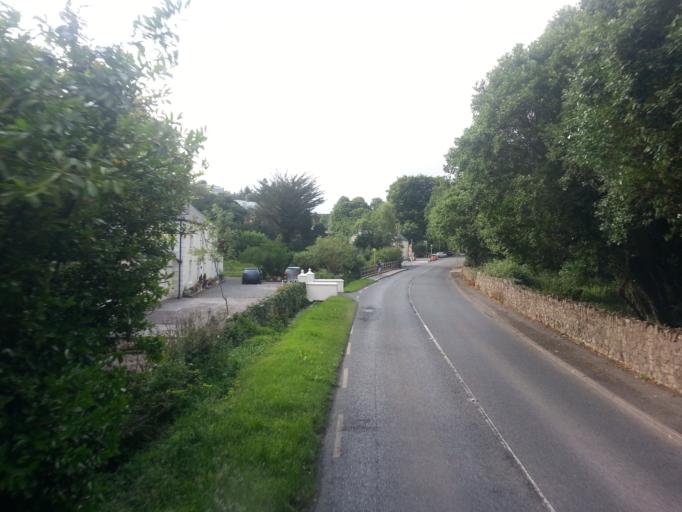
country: IE
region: Leinster
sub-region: Wicklow
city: Enniskerry
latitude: 53.2195
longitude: -6.1812
